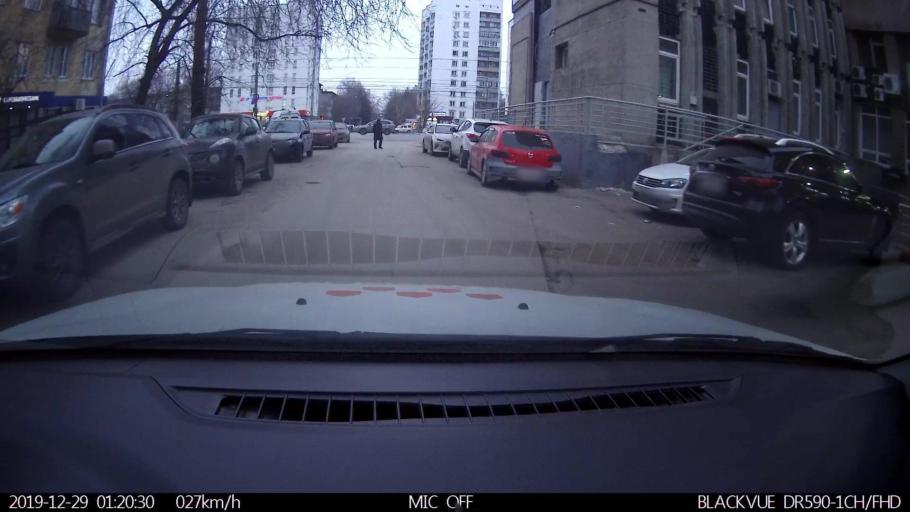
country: RU
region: Nizjnij Novgorod
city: Nizhniy Novgorod
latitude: 56.2760
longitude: 43.9199
